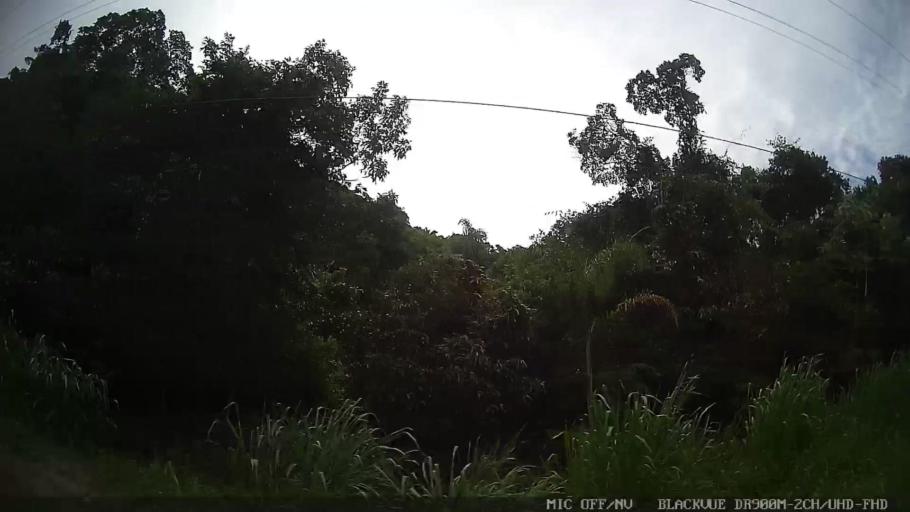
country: BR
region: Sao Paulo
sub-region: Iguape
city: Iguape
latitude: -24.6614
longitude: -47.4168
